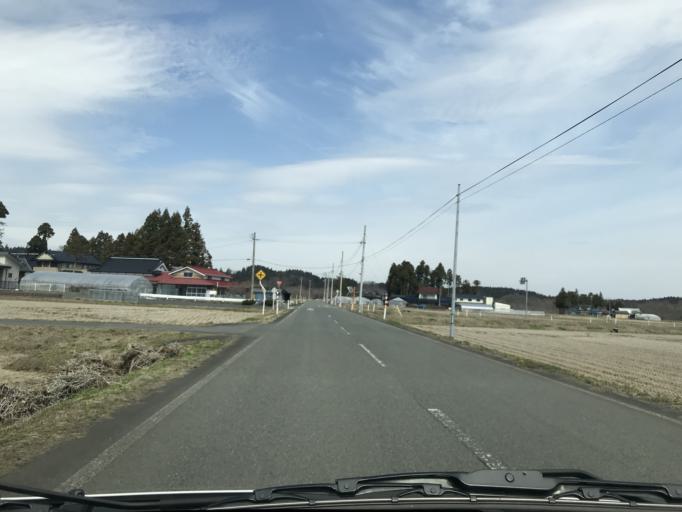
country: JP
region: Iwate
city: Mizusawa
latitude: 39.1441
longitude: 141.0570
